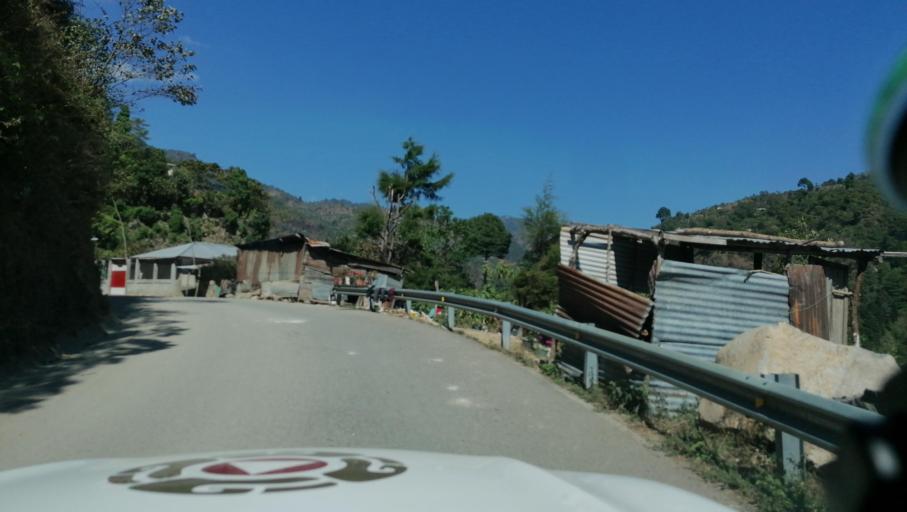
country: GT
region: San Marcos
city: Tacana
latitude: 15.1927
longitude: -92.1849
